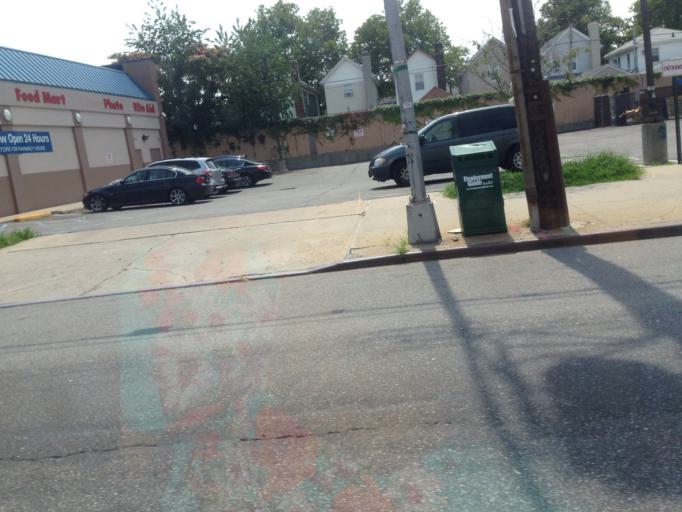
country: US
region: New York
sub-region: Kings County
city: Brooklyn
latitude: 40.6134
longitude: -73.9268
